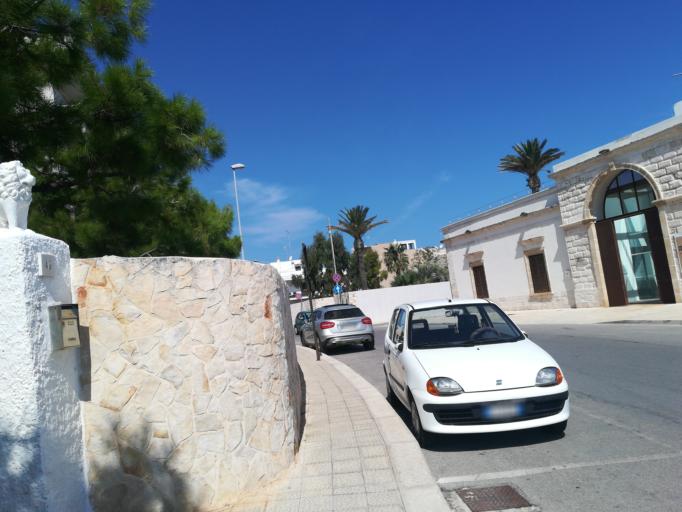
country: IT
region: Apulia
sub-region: Provincia di Bari
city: Polignano a Mare
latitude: 40.9937
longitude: 17.2287
